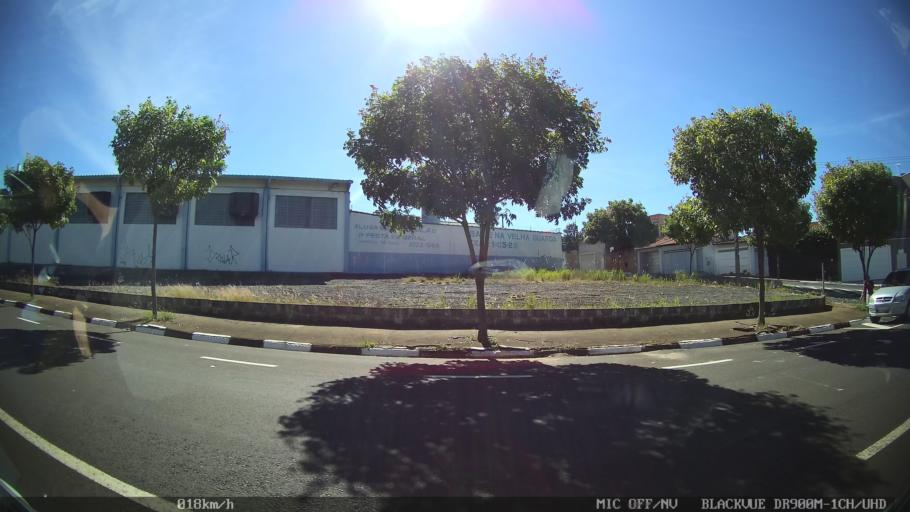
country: BR
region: Sao Paulo
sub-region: Franca
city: Franca
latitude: -20.5496
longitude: -47.3882
